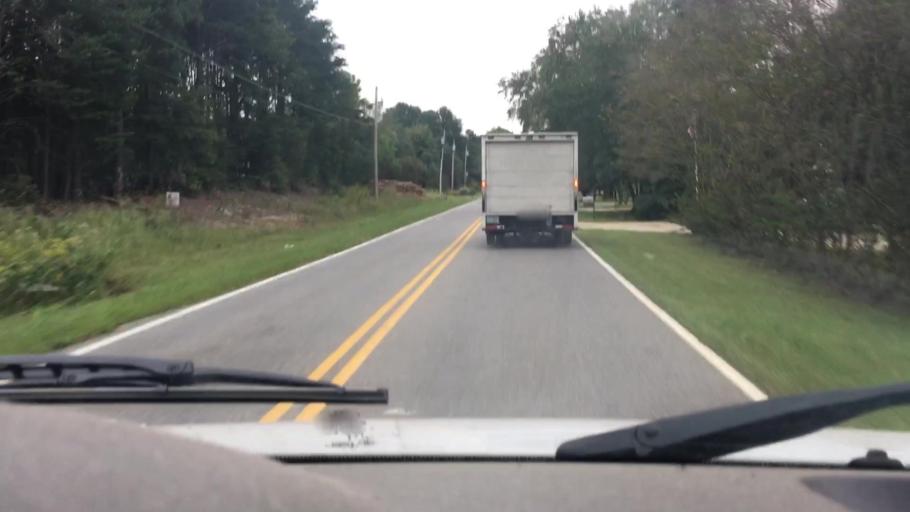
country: US
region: North Carolina
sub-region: Catawba County
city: Lake Norman of Catawba
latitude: 35.5605
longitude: -80.9905
